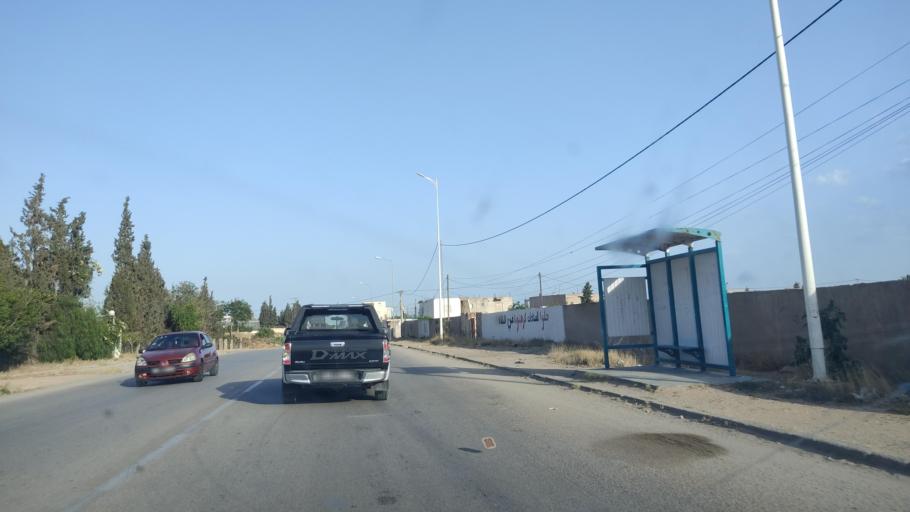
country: TN
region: Safaqis
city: Sfax
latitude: 34.7959
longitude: 10.6805
